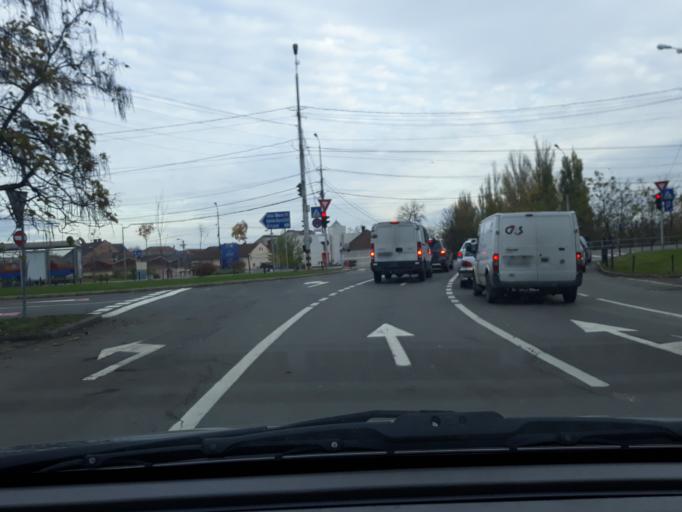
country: RO
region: Bihor
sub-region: Comuna Biharea
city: Oradea
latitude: 47.0655
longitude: 21.9220
